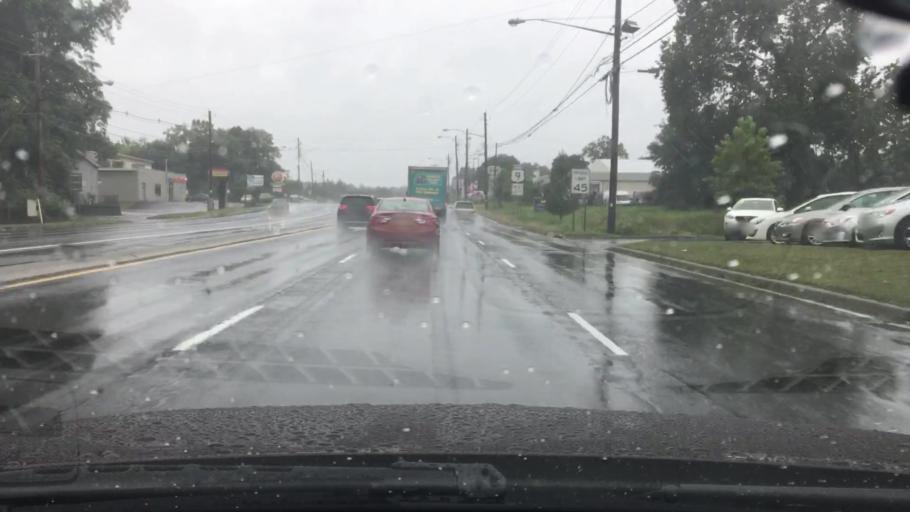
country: US
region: New York
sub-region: Dutchess County
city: Spackenkill
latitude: 41.6469
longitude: -73.9248
